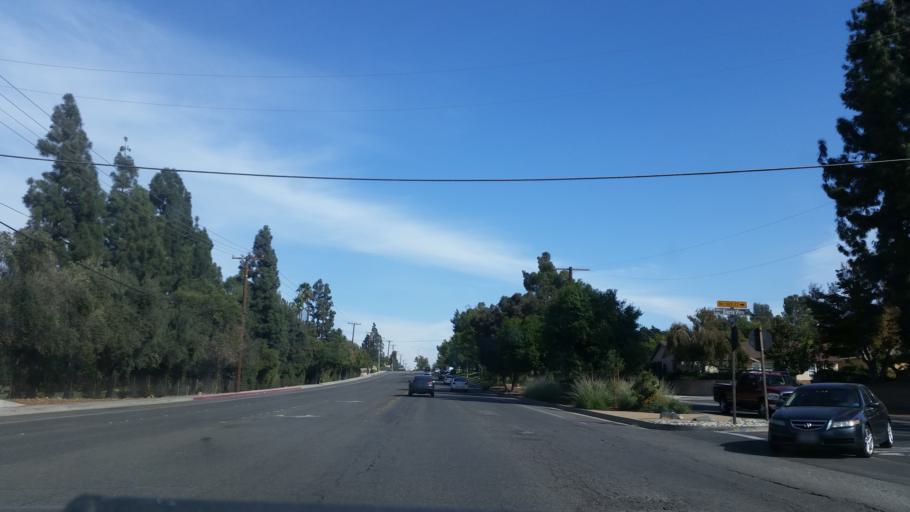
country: US
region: California
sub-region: Los Angeles County
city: San Dimas
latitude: 34.1262
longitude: -117.8161
